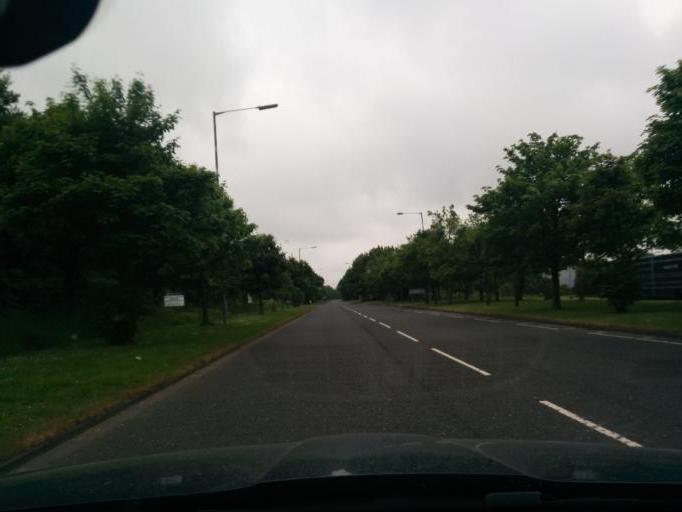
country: GB
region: England
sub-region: Northumberland
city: Cramlington
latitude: 55.0958
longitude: -1.6009
